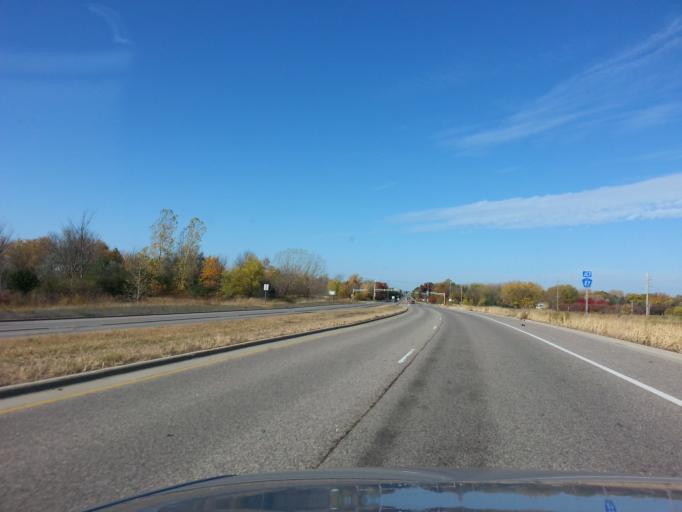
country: US
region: Minnesota
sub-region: Scott County
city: Prior Lake
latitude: 44.6937
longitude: -93.3756
